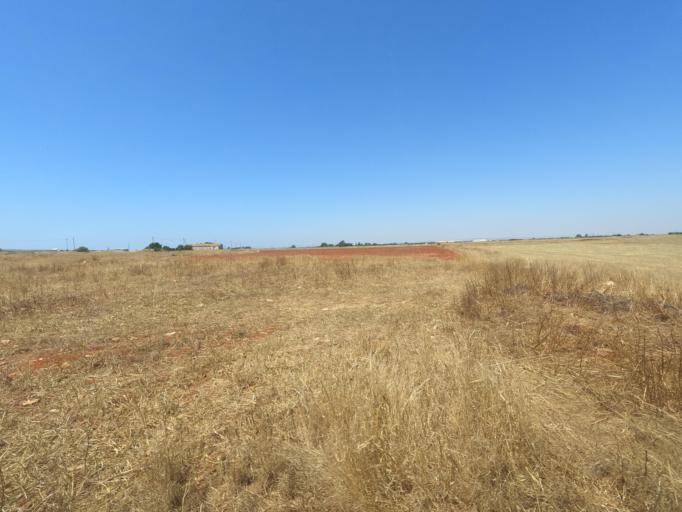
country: CY
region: Ammochostos
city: Liopetri
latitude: 35.0285
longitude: 33.8884
